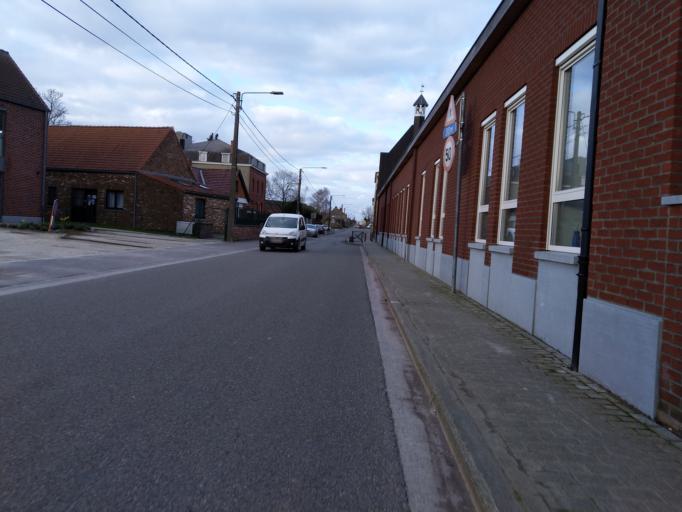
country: BE
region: Wallonia
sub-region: Province du Hainaut
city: Jurbise
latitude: 50.5638
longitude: 3.9838
